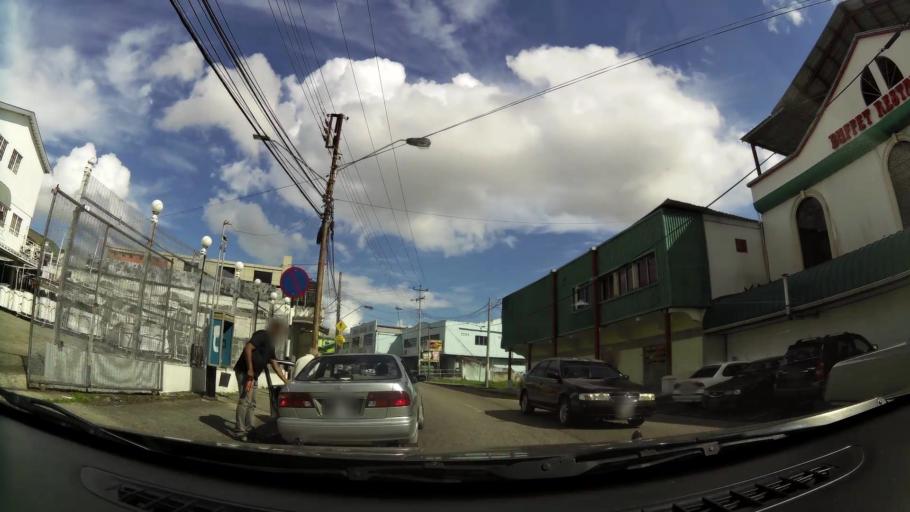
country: TT
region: City of San Fernando
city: San Fernando
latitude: 10.2771
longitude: -61.4586
